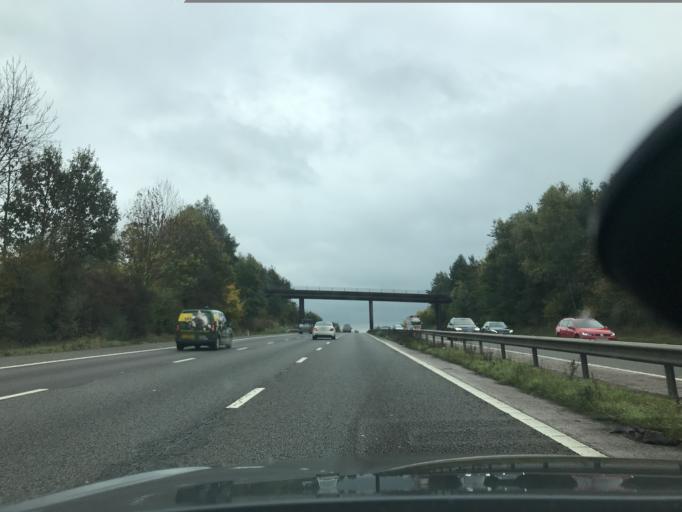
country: GB
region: England
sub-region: Warwickshire
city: Henley in Arden
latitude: 52.3288
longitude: -1.7431
